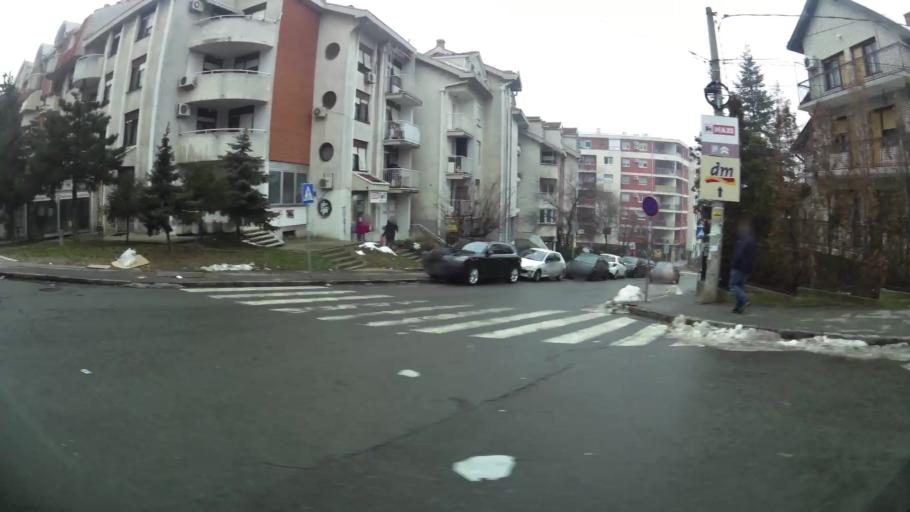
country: RS
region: Central Serbia
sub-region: Belgrade
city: Cukarica
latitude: 44.7737
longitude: 20.4181
